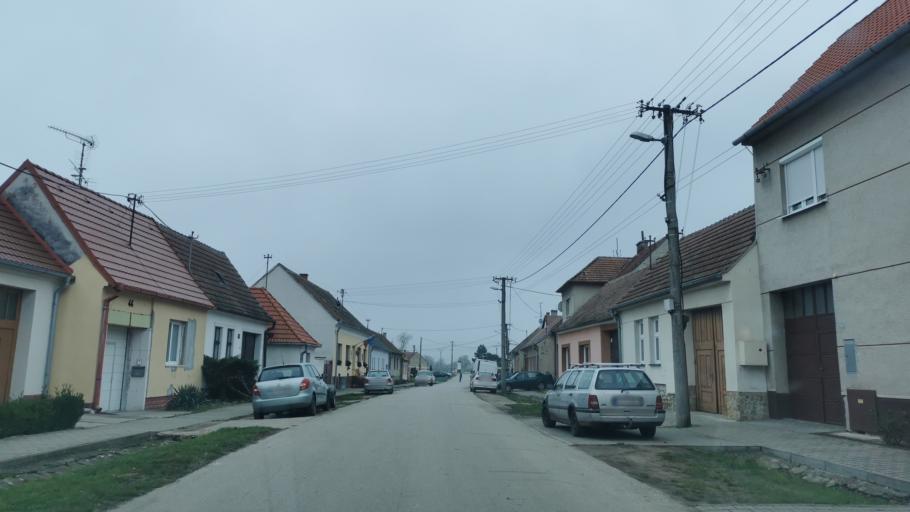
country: SK
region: Trnavsky
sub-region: Okres Skalica
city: Holic
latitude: 48.8323
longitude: 17.1700
